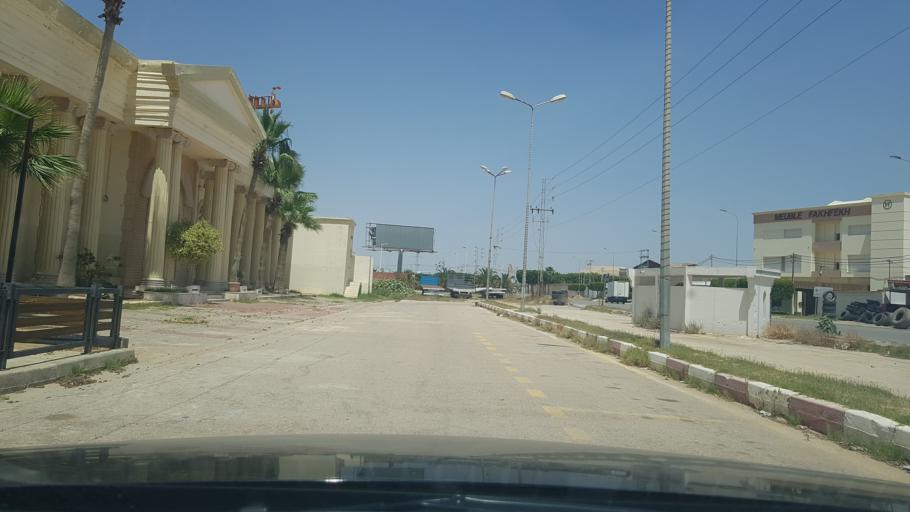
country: TN
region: Safaqis
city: Al Qarmadah
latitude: 34.8440
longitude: 10.7624
